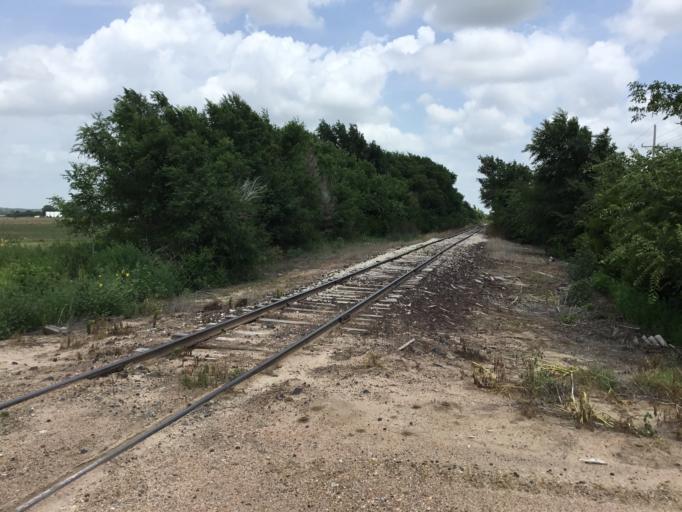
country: US
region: Kansas
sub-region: Pratt County
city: Pratt
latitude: 37.6501
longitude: -98.5201
